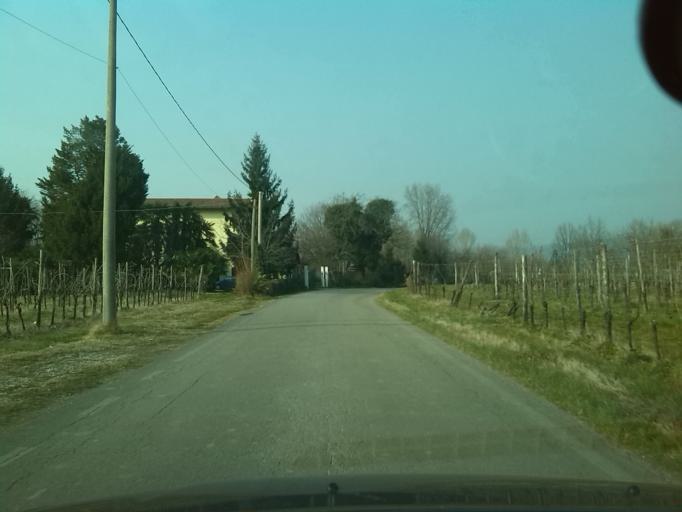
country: IT
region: Friuli Venezia Giulia
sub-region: Provincia di Gorizia
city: Cormons
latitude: 45.9413
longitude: 13.4727
